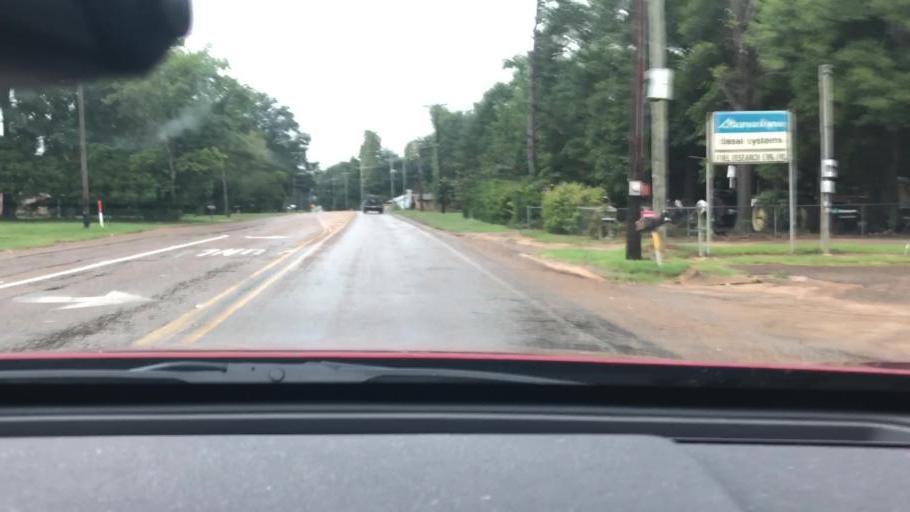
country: US
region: Texas
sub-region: Bowie County
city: Nash
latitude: 33.4425
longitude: -94.1309
